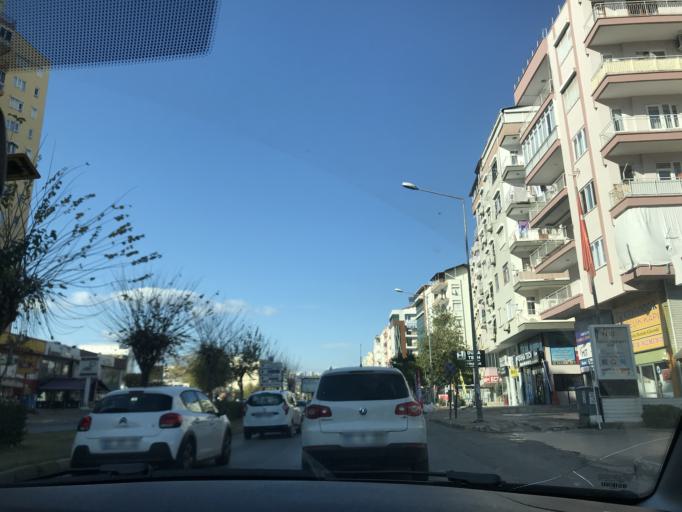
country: TR
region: Antalya
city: Antalya
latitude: 36.9063
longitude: 30.7000
